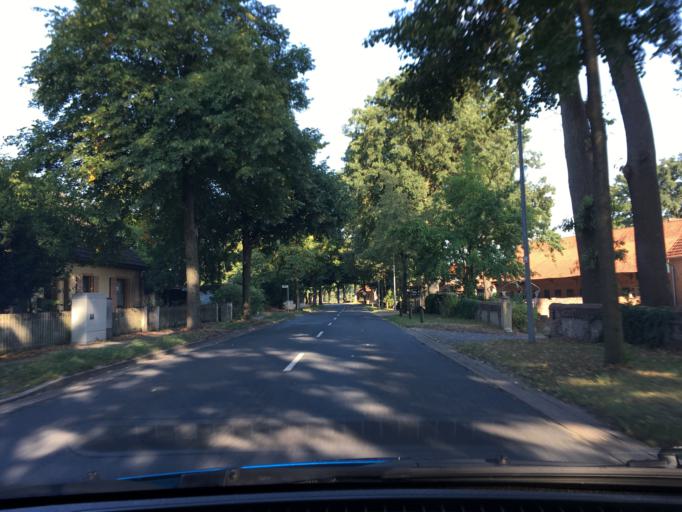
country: DE
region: Lower Saxony
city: Isernhagen Farster Bauerschaft
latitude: 52.4782
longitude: 9.9151
